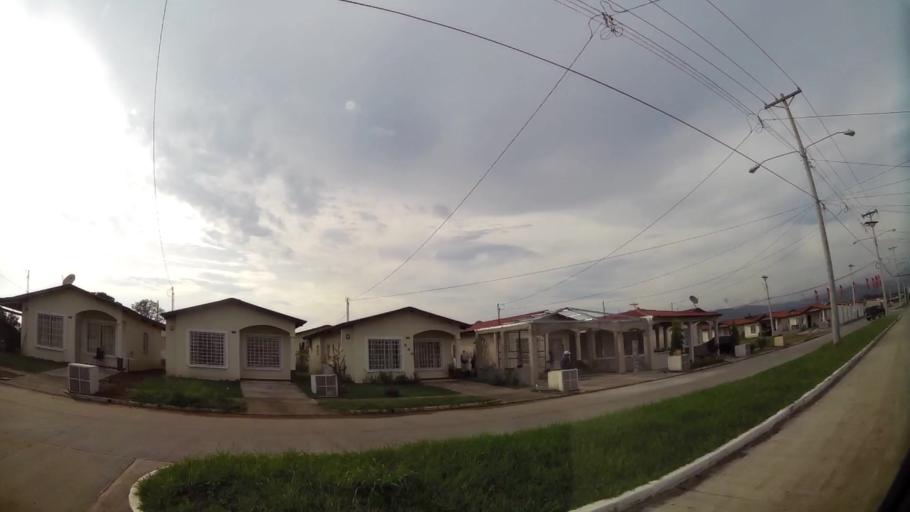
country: PA
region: Panama
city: Tocumen
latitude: 9.0687
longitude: -79.3651
